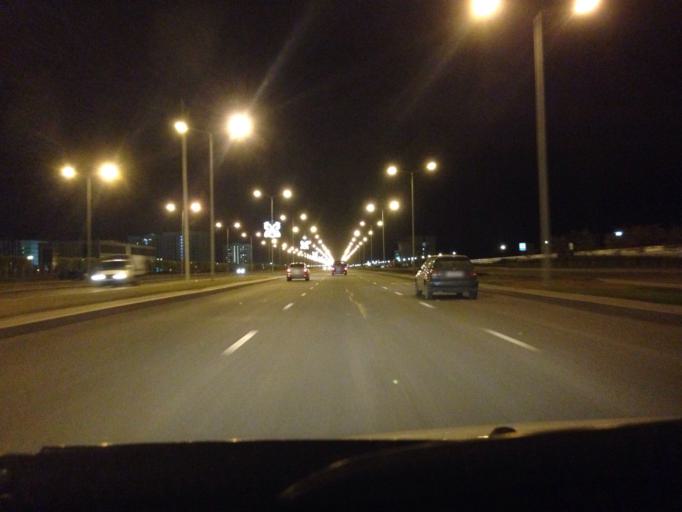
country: KZ
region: Astana Qalasy
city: Astana
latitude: 51.0990
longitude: 71.3945
